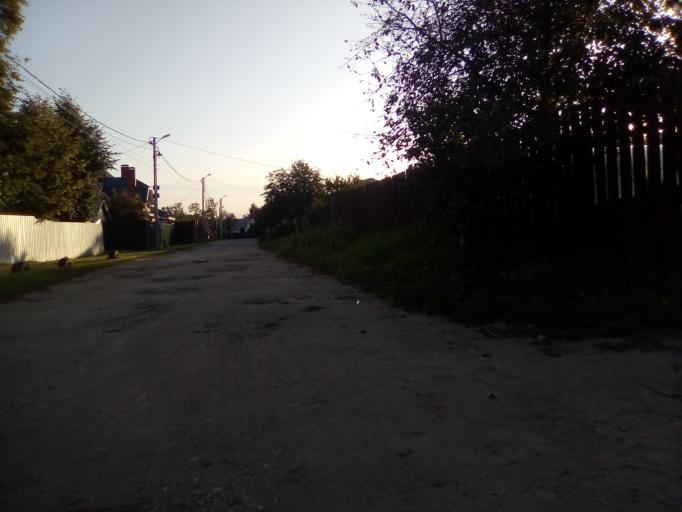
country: RU
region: Moskovskaya
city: Krasnoznamensk
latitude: 55.5743
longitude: 37.0322
